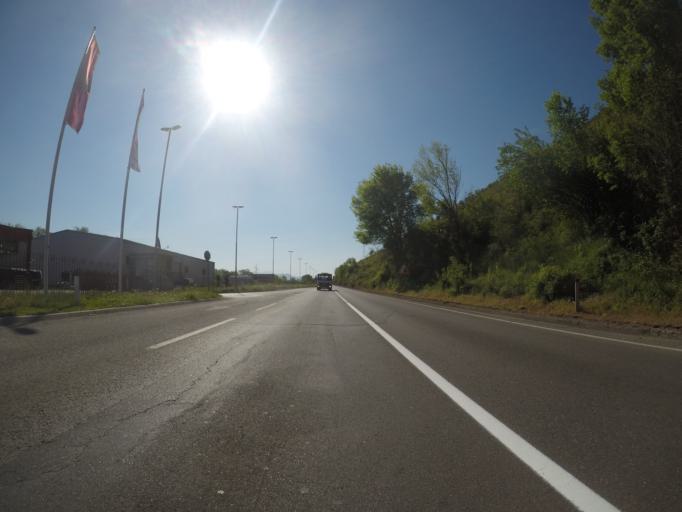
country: ME
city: Spuz
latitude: 42.4523
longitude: 19.1958
